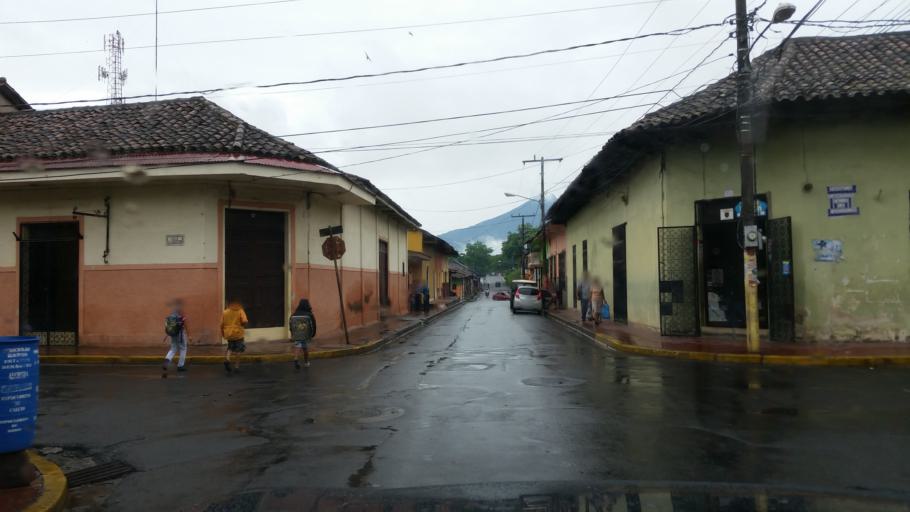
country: NI
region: Granada
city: Granada
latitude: 11.9274
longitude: -85.9574
